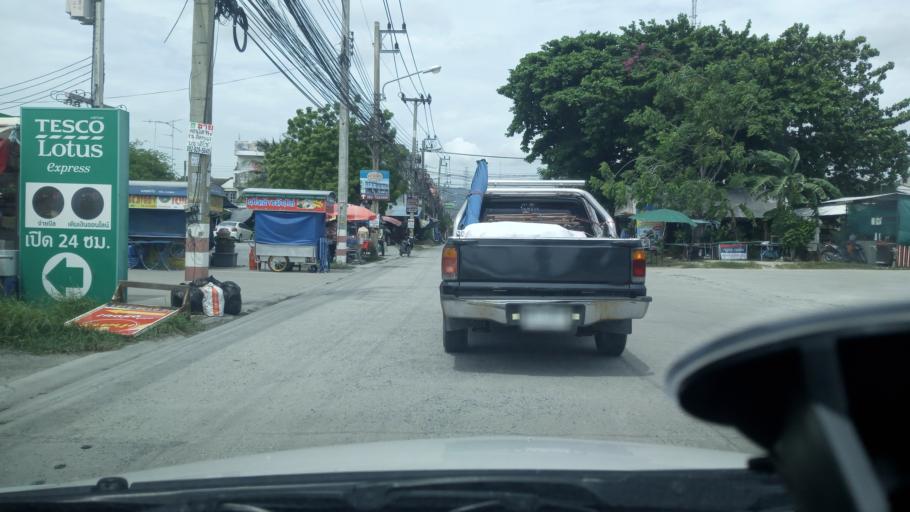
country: TH
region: Chon Buri
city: Chon Buri
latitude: 13.2977
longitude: 100.9496
